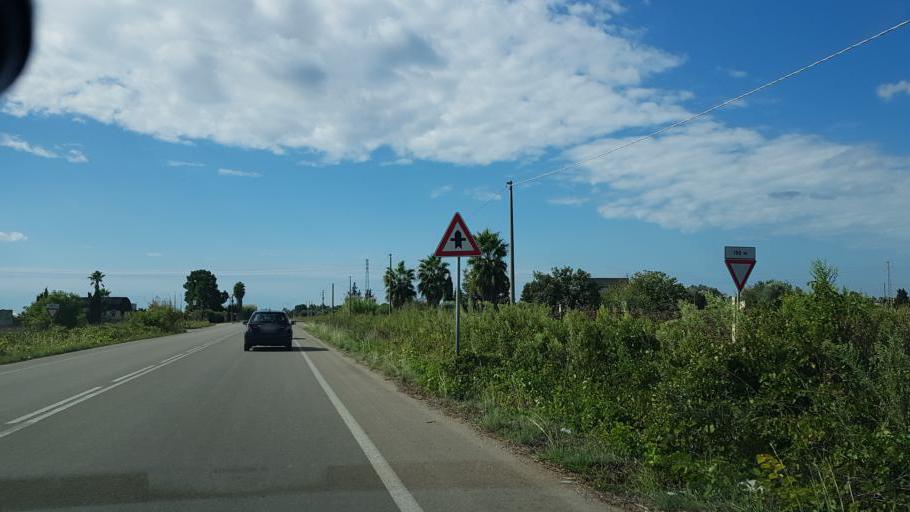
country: IT
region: Apulia
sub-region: Provincia di Lecce
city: Leverano
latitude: 40.3052
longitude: 18.0145
